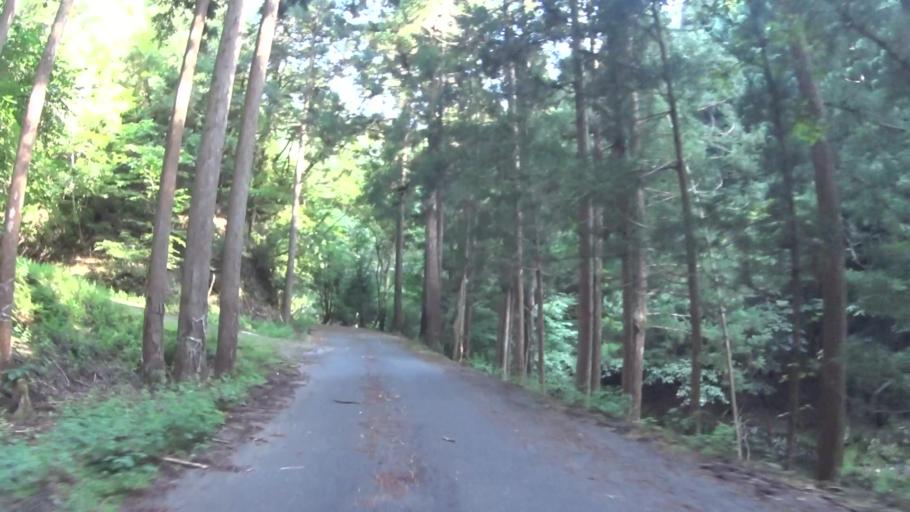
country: JP
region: Fukui
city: Obama
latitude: 35.2684
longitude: 135.6966
